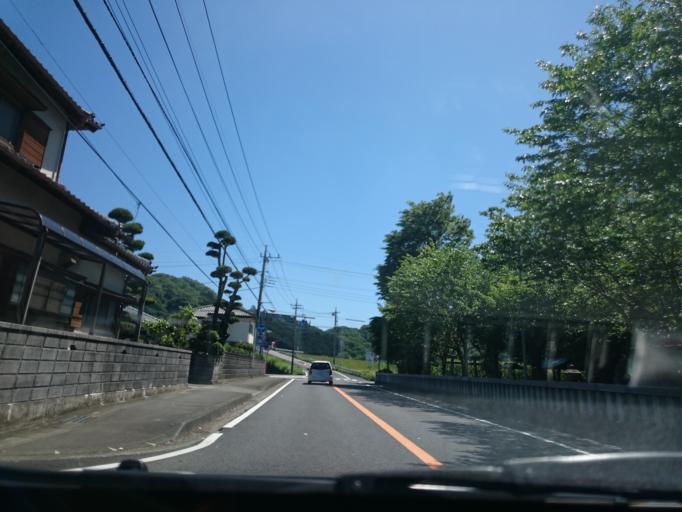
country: JP
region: Shizuoka
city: Mishima
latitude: 35.0714
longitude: 138.9309
